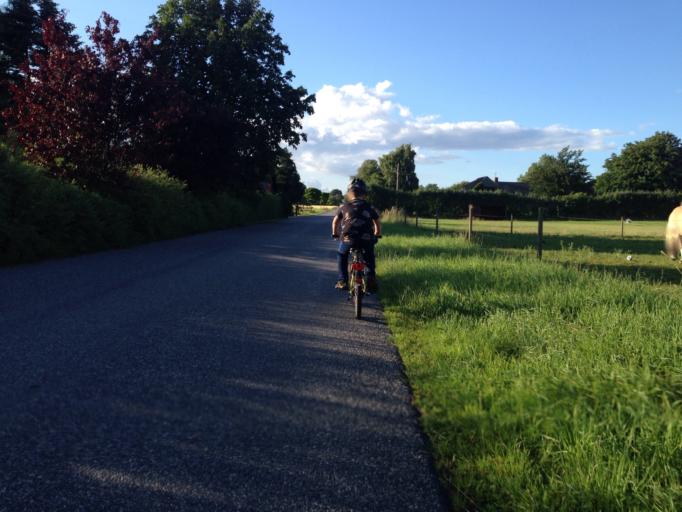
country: DK
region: South Denmark
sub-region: Middelfart Kommune
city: Norre Aby
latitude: 55.4743
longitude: 9.9034
